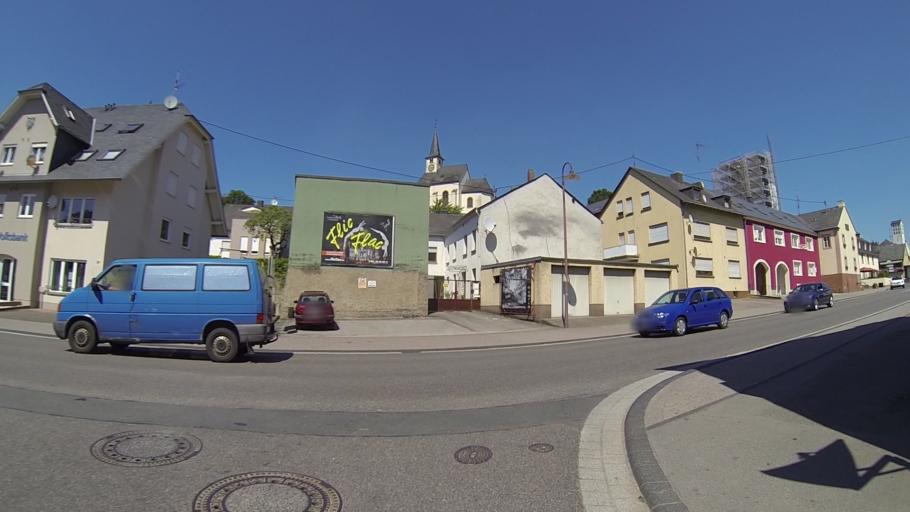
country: DE
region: Rheinland-Pfalz
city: Wasserliesch
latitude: 49.7088
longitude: 6.5487
